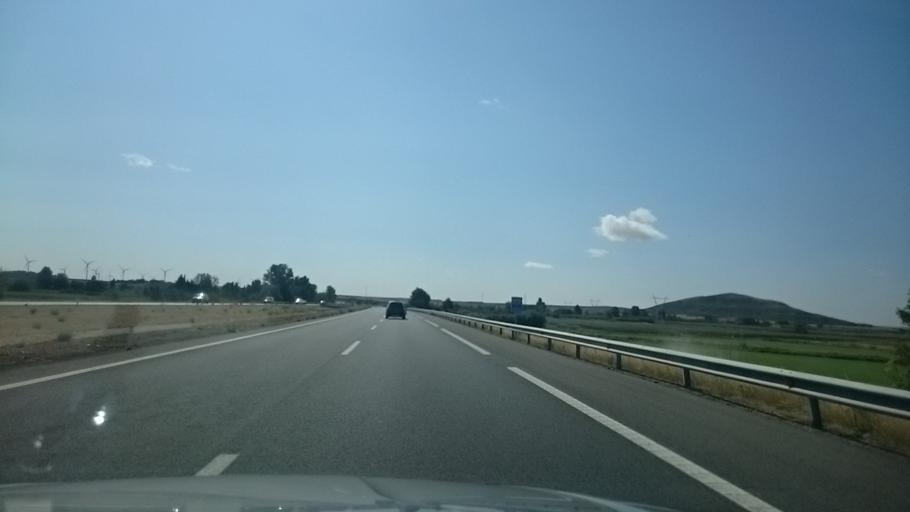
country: ES
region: Aragon
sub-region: Provincia de Zaragoza
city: Frescano
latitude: 41.8980
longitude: -1.4396
